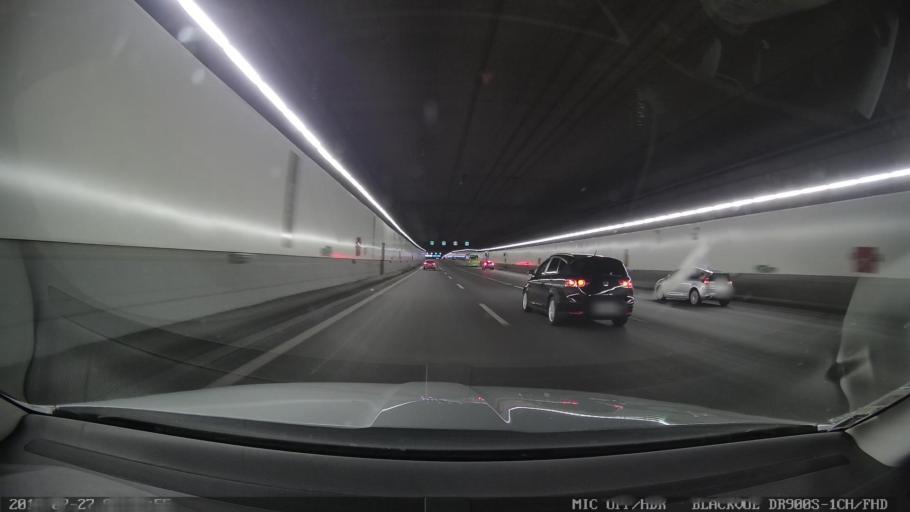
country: ES
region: Madrid
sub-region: Provincia de Madrid
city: Moncloa-Aravaca
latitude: 40.4129
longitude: -3.7324
